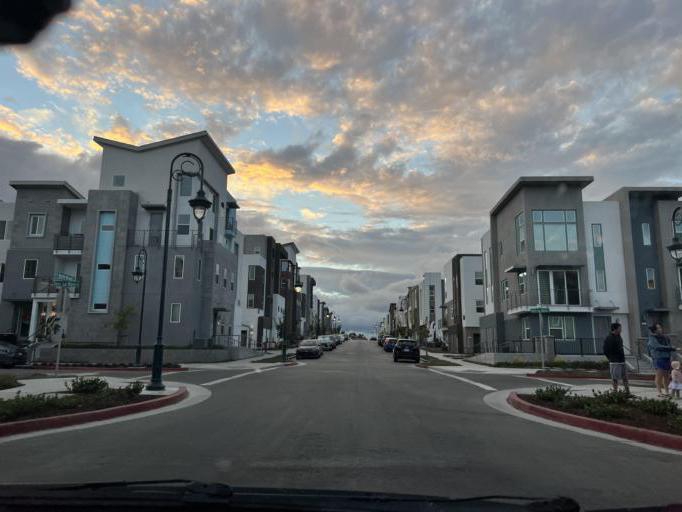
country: US
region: California
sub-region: Santa Clara County
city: Seven Trees
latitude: 37.2854
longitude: -121.8514
